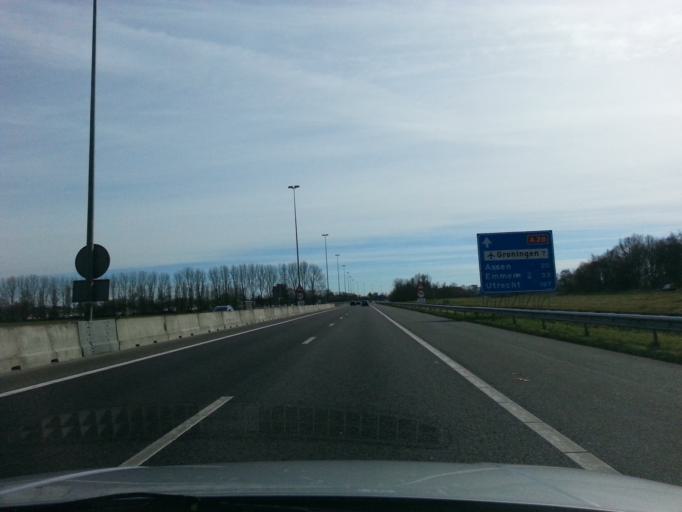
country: NL
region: Groningen
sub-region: Gemeente Haren
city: Haren
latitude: 53.1756
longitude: 6.5850
